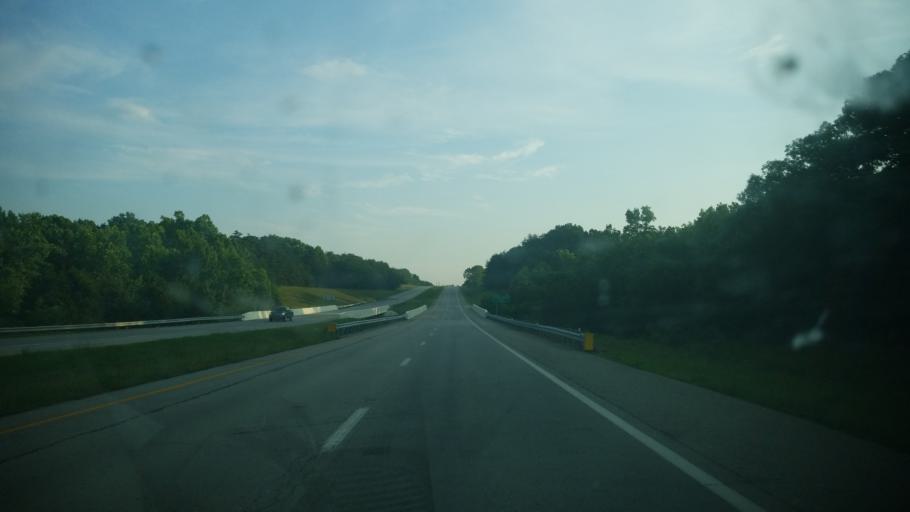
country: US
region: Ohio
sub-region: Adams County
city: Peebles
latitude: 38.9706
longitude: -83.3461
